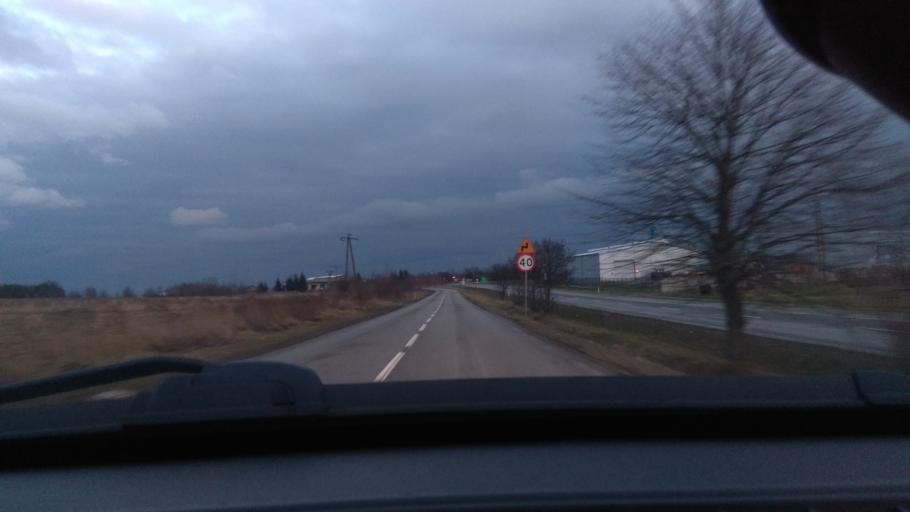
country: PL
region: Greater Poland Voivodeship
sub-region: Powiat kepinski
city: Kepno
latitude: 51.2883
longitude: 18.0093
